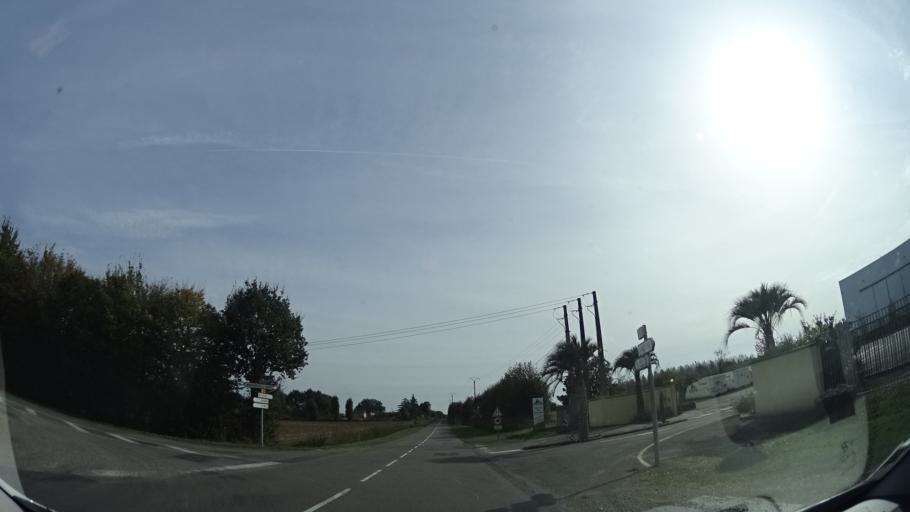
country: FR
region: Brittany
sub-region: Departement d'Ille-et-Vilaine
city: La Meziere
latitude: 48.2180
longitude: -1.7394
